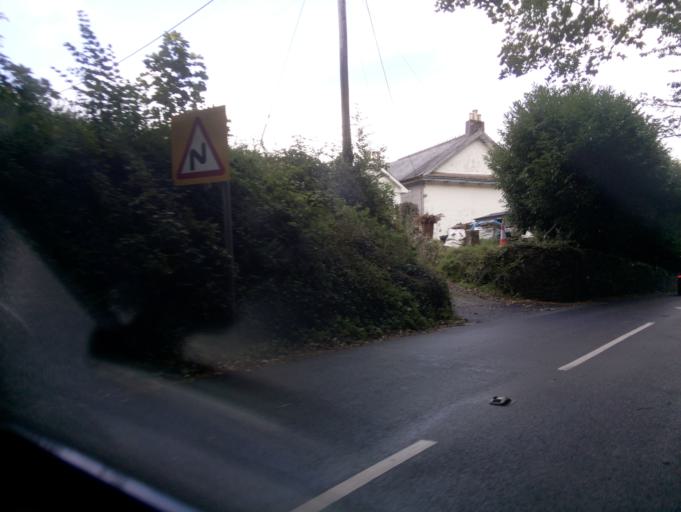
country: GB
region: England
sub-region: Devon
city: Modbury
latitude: 50.3496
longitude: -3.9018
